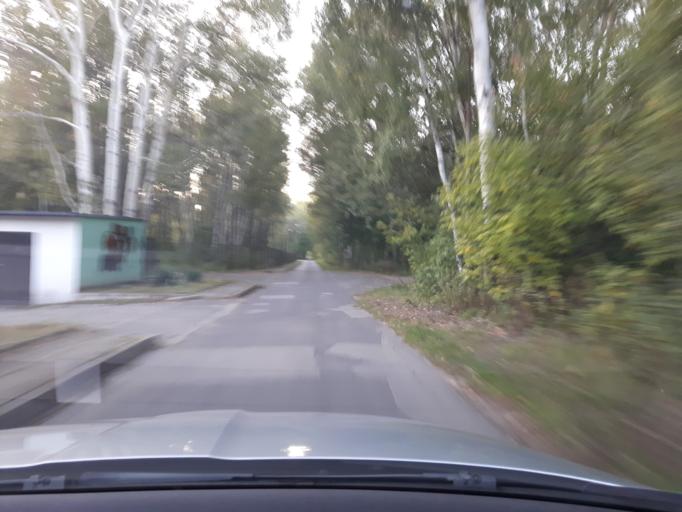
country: PL
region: Masovian Voivodeship
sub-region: Powiat wolominski
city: Kobylka
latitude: 52.3466
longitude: 21.1822
